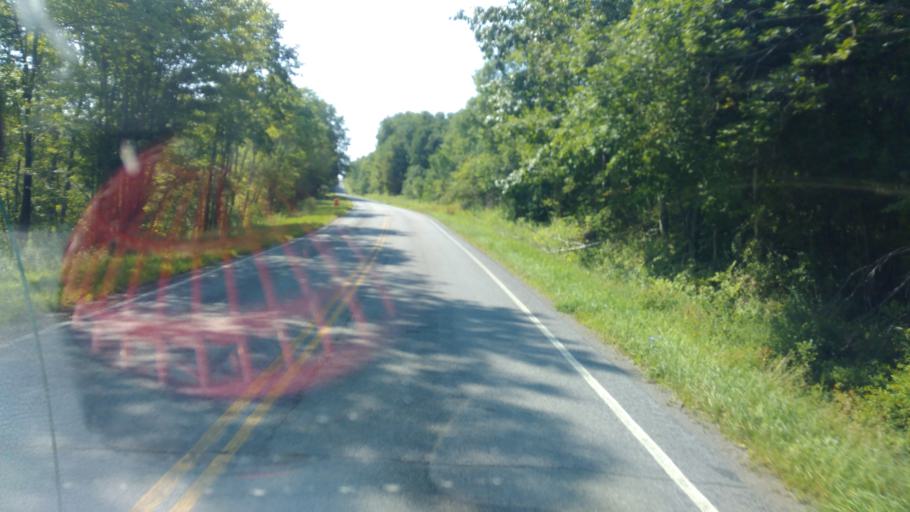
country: US
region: New York
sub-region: Allegany County
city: Friendship
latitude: 42.1681
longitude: -78.1504
